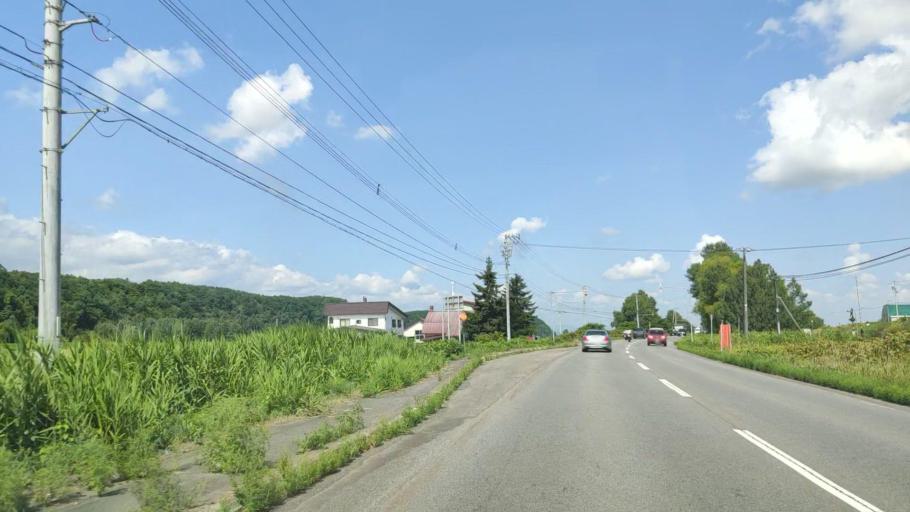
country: JP
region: Hokkaido
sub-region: Asahikawa-shi
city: Asahikawa
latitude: 43.6322
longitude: 142.4588
